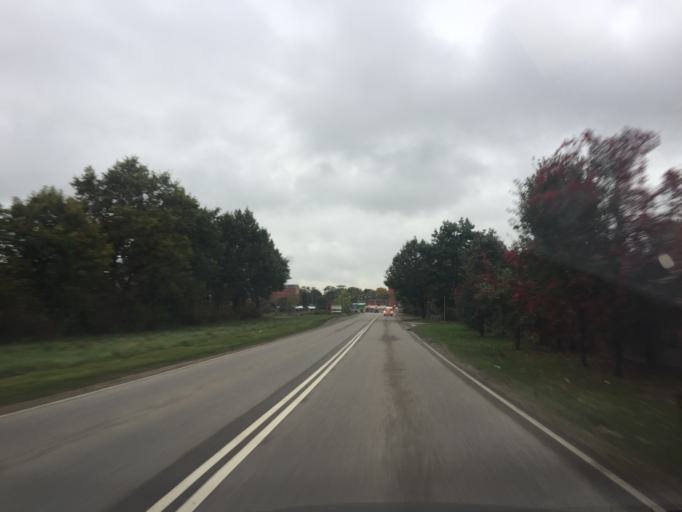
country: DK
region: Capital Region
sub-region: Hoje-Taastrup Kommune
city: Flong
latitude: 55.6464
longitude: 12.1901
